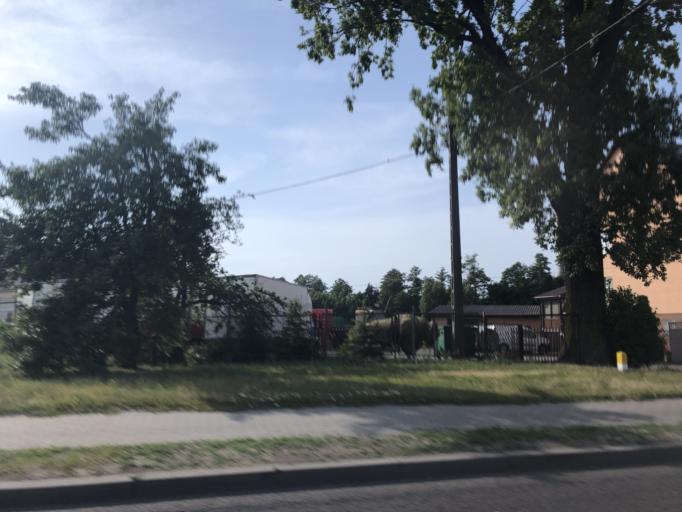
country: PL
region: Podlasie
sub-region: Lomza
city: Lomza
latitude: 53.1633
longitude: 22.0362
